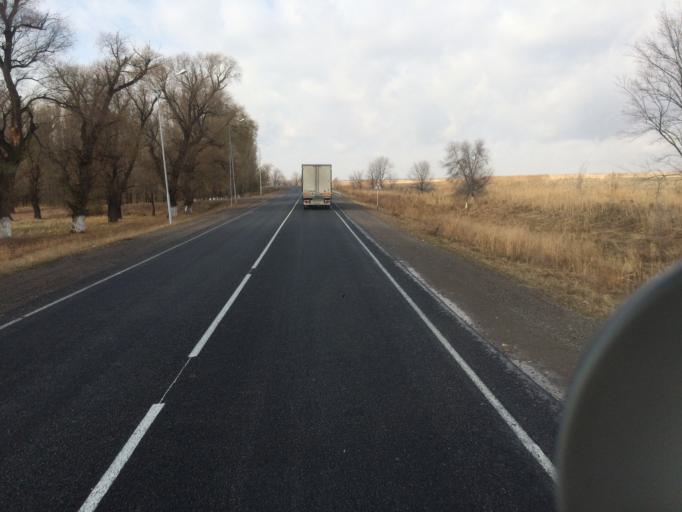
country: KZ
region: Zhambyl
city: Georgiyevka
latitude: 43.2220
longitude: 74.4512
